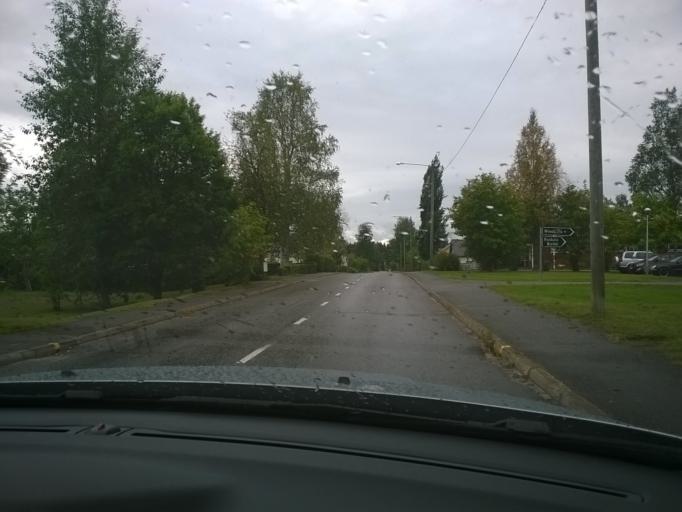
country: FI
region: Kainuu
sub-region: Kehys-Kainuu
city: Kuhmo
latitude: 64.1261
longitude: 29.5210
